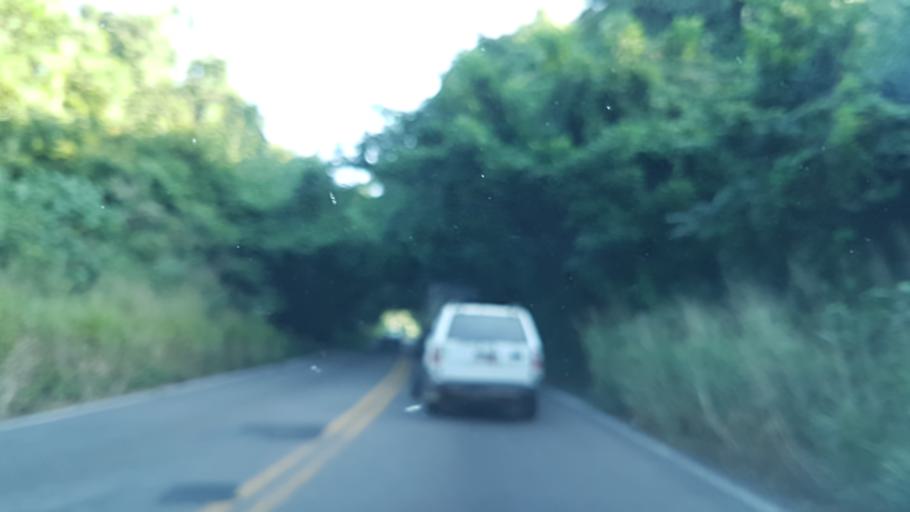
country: MX
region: Nayarit
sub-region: Bahia de Banderas
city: Lo de Marcos
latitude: 20.8810
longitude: -105.4212
